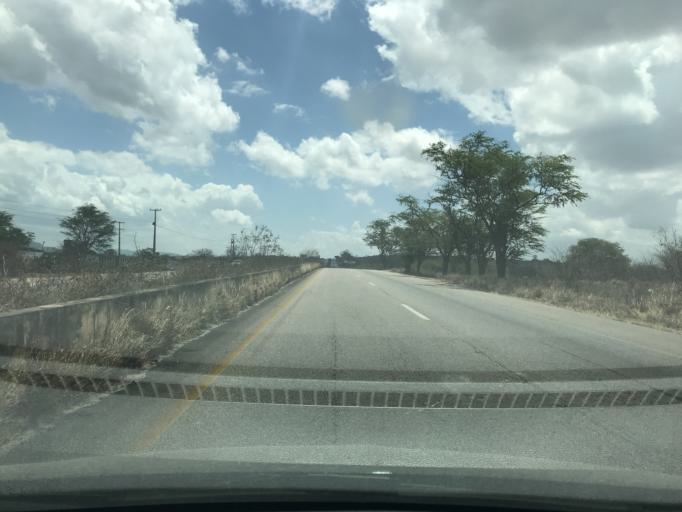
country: BR
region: Pernambuco
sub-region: Caruaru
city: Caruaru
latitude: -8.3019
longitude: -35.9180
